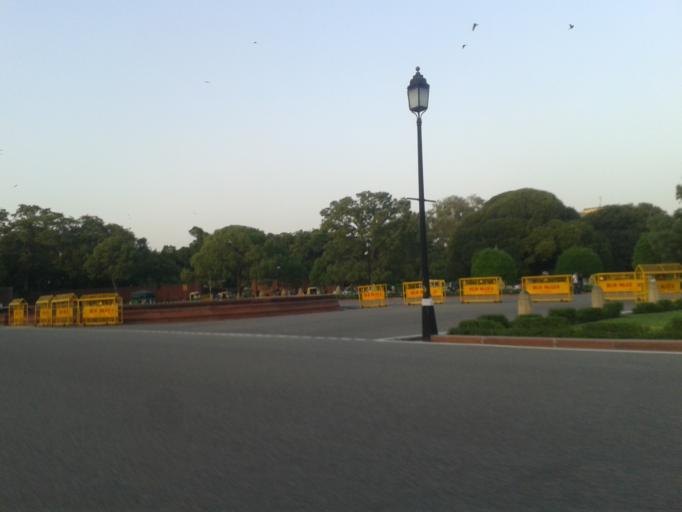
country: IN
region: NCT
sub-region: New Delhi
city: New Delhi
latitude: 28.6148
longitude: 77.2088
